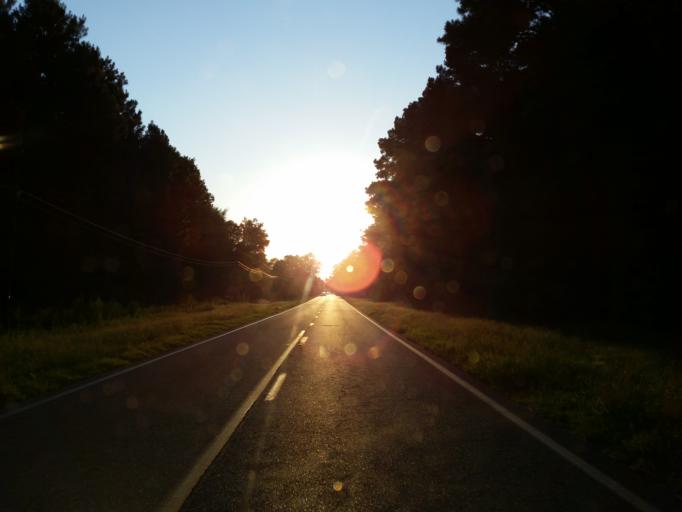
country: US
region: Georgia
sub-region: Berrien County
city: Nashville
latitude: 31.2018
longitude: -83.2317
